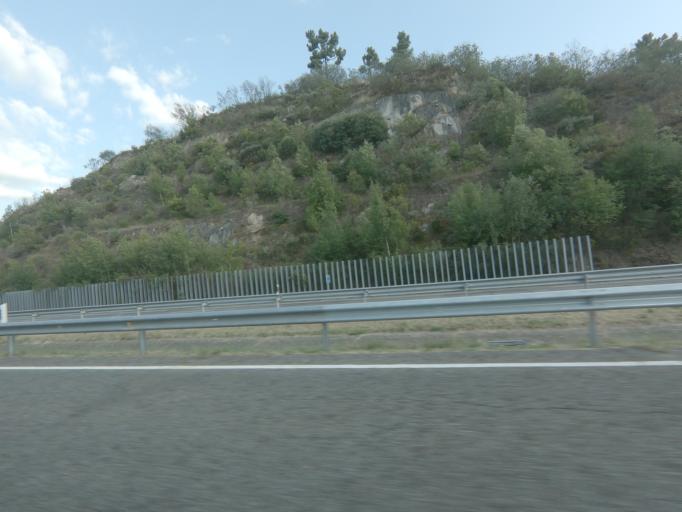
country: ES
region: Galicia
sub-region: Provincia de Ourense
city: Oimbra
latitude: 41.9258
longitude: -7.4893
